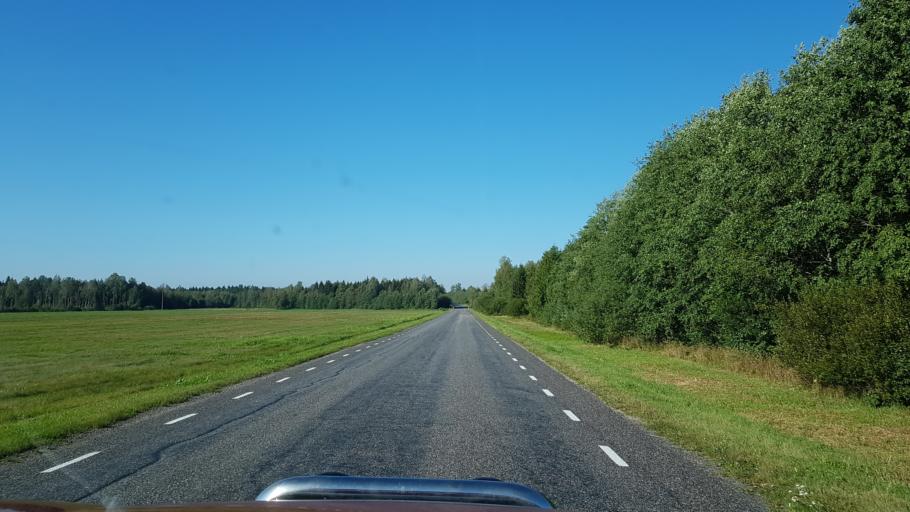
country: EE
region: Jogevamaa
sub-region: Jogeva linn
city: Jogeva
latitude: 58.6965
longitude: 26.3791
